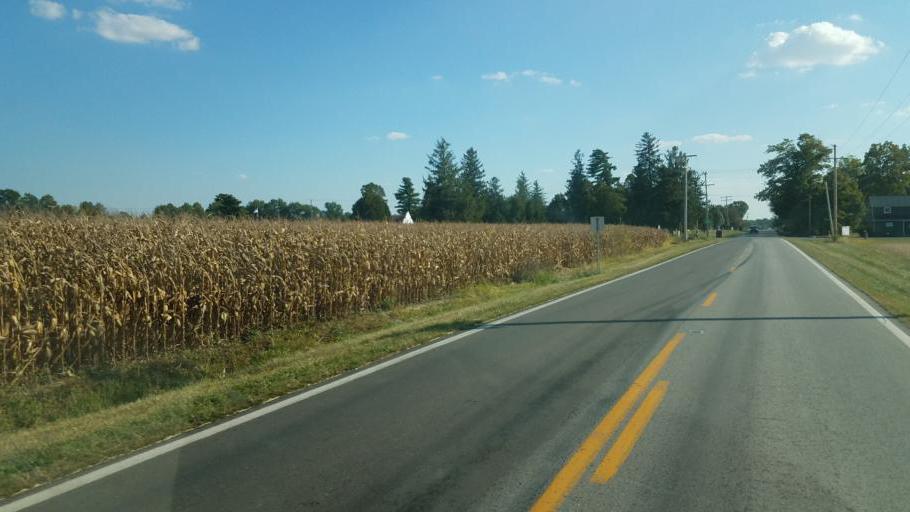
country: US
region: Ohio
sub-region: Union County
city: Richwood
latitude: 40.6014
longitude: -83.3805
